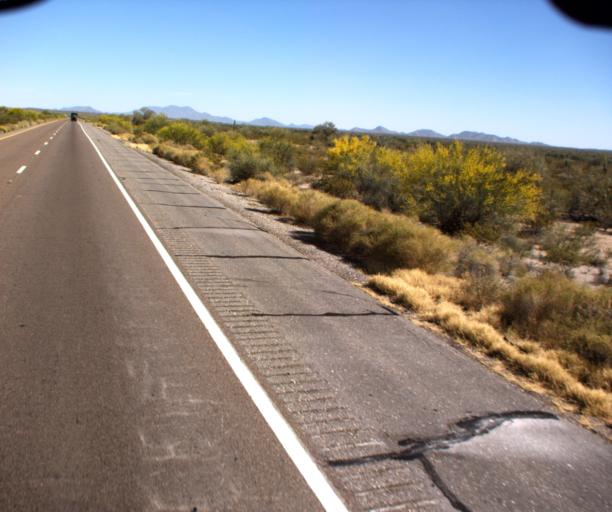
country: US
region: Arizona
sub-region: Maricopa County
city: Gila Bend
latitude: 32.8543
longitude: -112.3722
